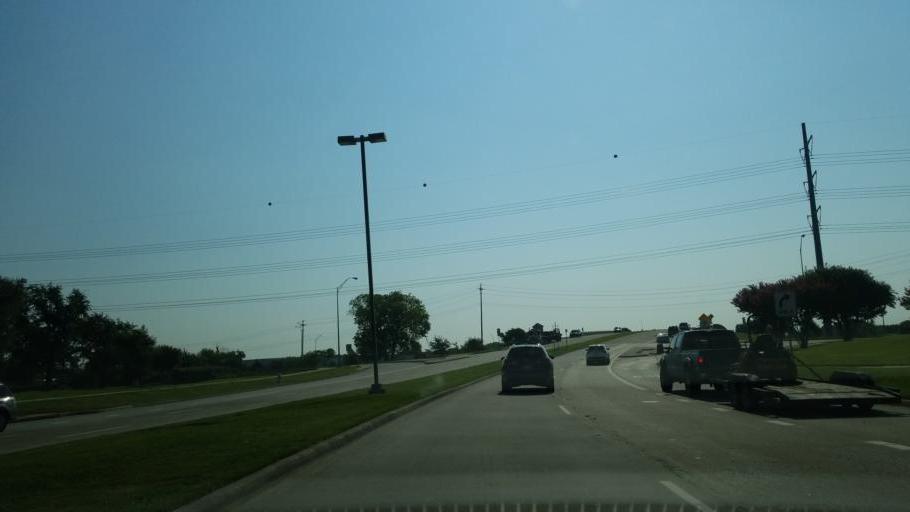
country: US
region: Texas
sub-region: Collin County
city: Allen
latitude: 33.1176
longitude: -96.6727
